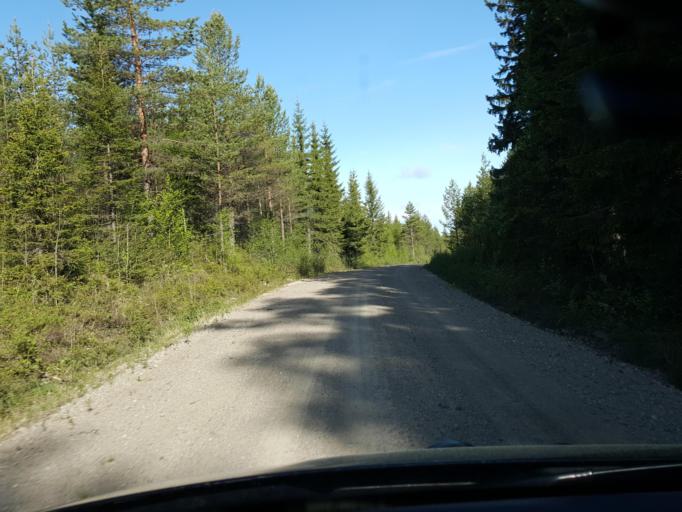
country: SE
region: Vaesternorrland
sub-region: Ange Kommun
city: Ange
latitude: 62.1854
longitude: 15.6068
